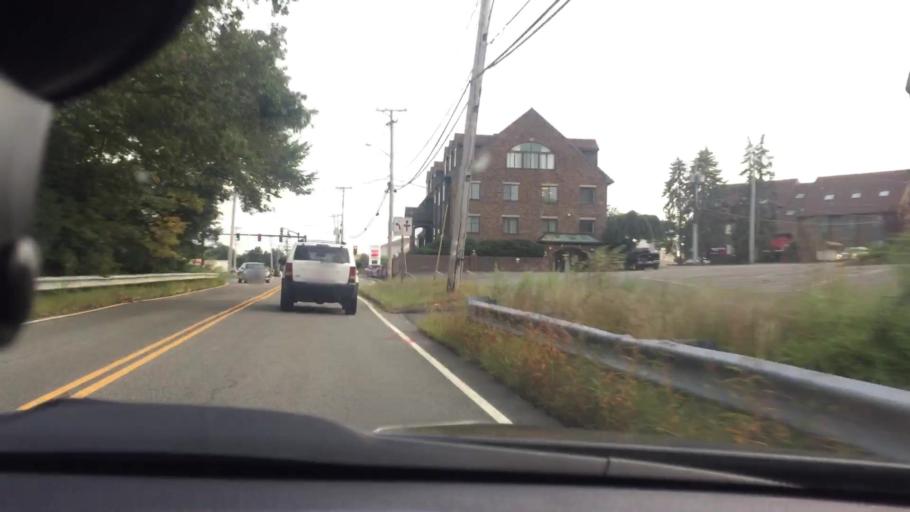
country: US
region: Massachusetts
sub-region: Norfolk County
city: Randolph
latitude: 42.1549
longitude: -71.0736
